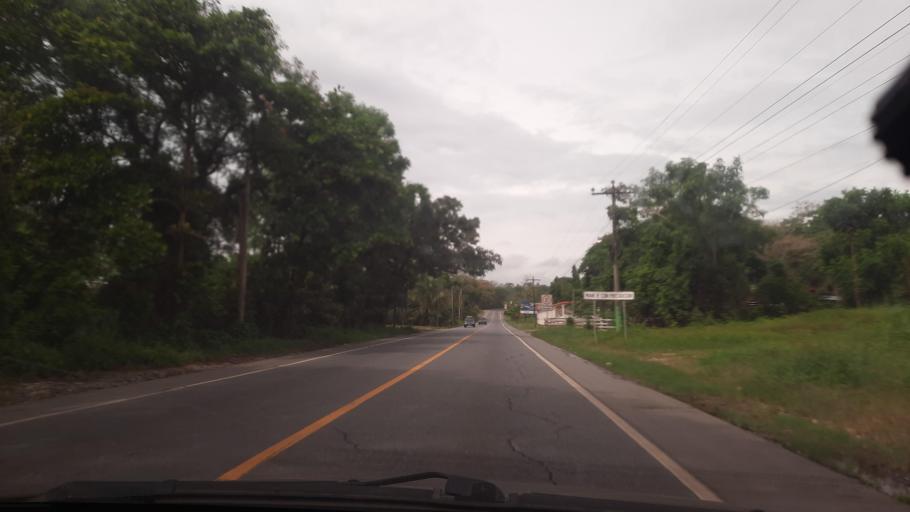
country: GT
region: Izabal
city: Morales
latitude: 15.5190
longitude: -88.7977
